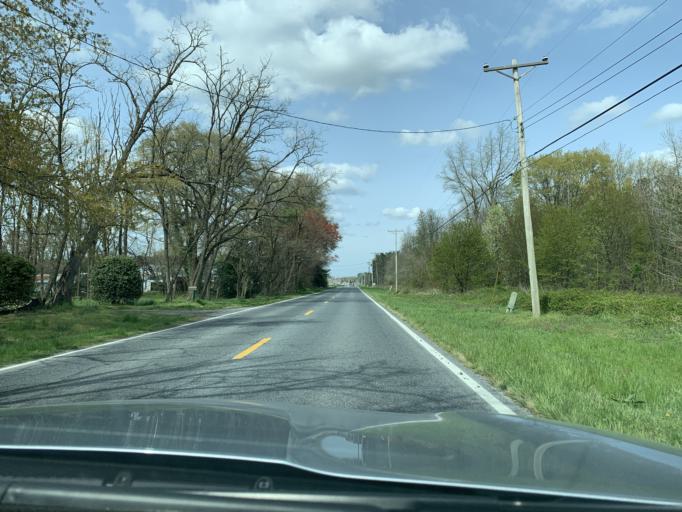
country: US
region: Delaware
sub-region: Sussex County
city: Georgetown
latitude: 38.6571
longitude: -75.3810
